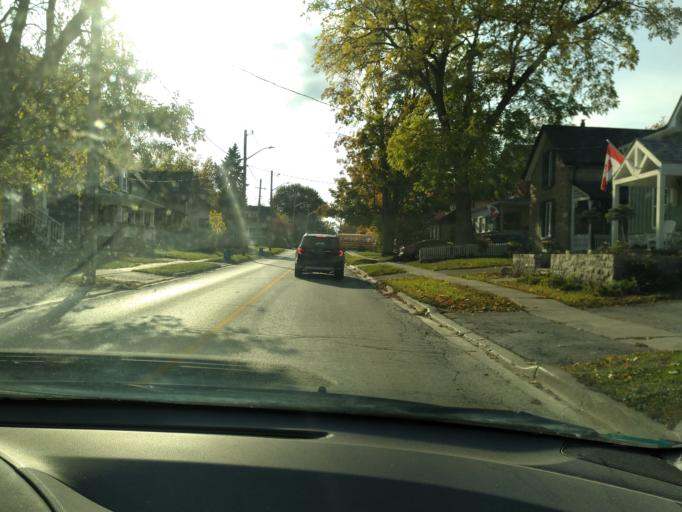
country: CA
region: Ontario
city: Newmarket
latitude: 44.0558
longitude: -79.4610
